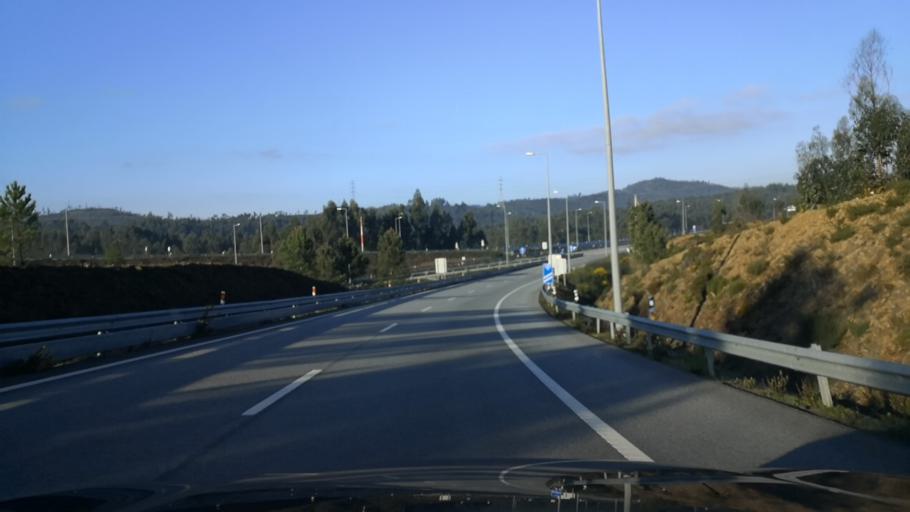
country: PT
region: Porto
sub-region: Valongo
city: Sobrado
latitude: 41.2311
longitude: -8.4561
